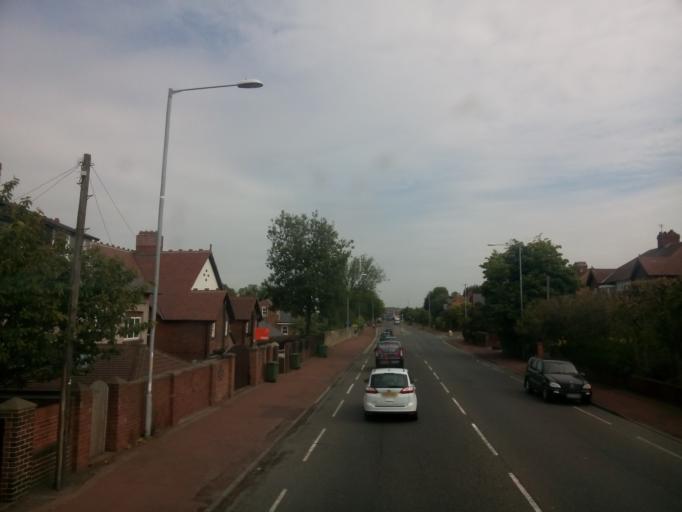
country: GB
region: England
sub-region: Gateshead
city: Gateshead
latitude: 54.9424
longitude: -1.5996
